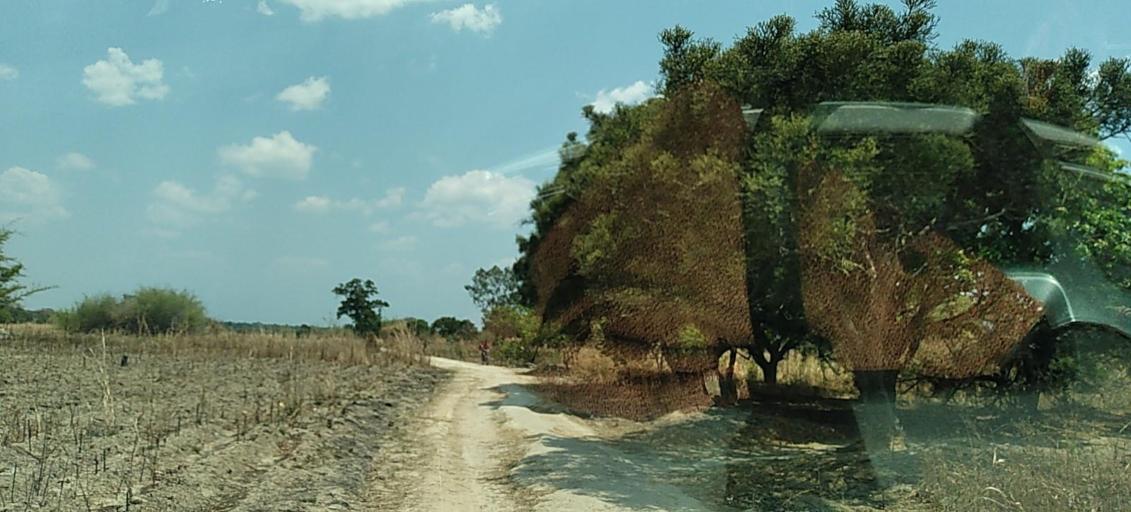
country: ZM
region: Copperbelt
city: Chililabombwe
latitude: -12.4826
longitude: 27.6692
